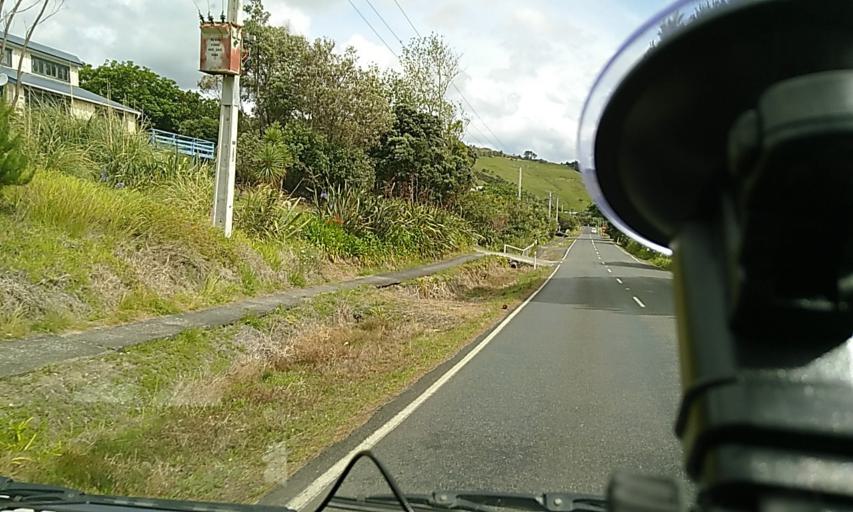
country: NZ
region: Northland
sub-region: Far North District
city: Ahipara
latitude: -35.5261
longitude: 173.3898
